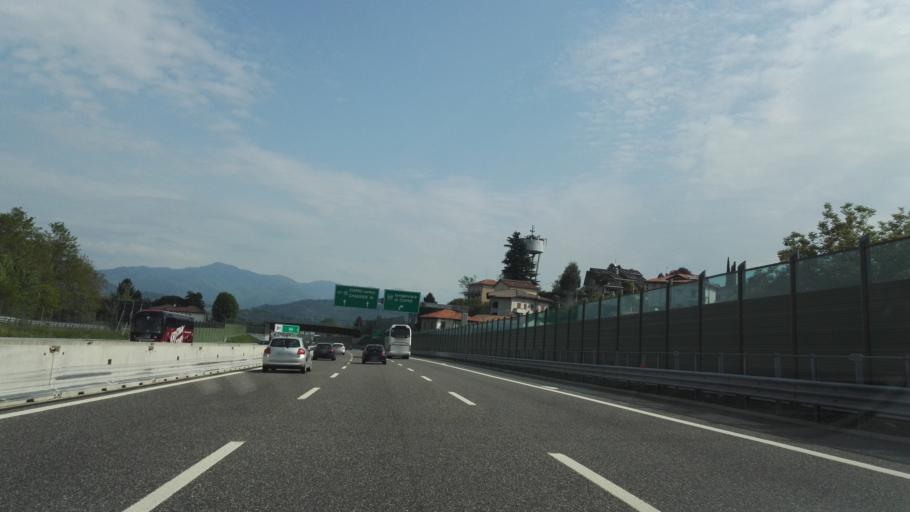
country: IT
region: Lombardy
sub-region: Provincia di Como
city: Luisago
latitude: 45.7569
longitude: 9.0440
